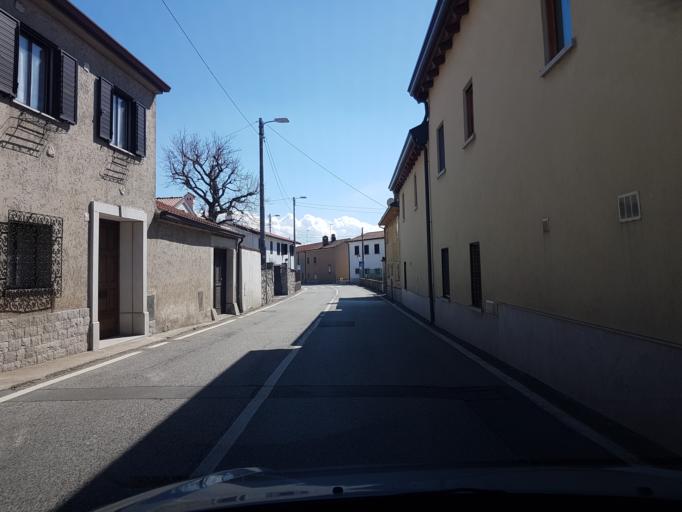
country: IT
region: Friuli Venezia Giulia
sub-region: Provincia di Trieste
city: Domio
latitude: 45.6583
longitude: 13.8390
